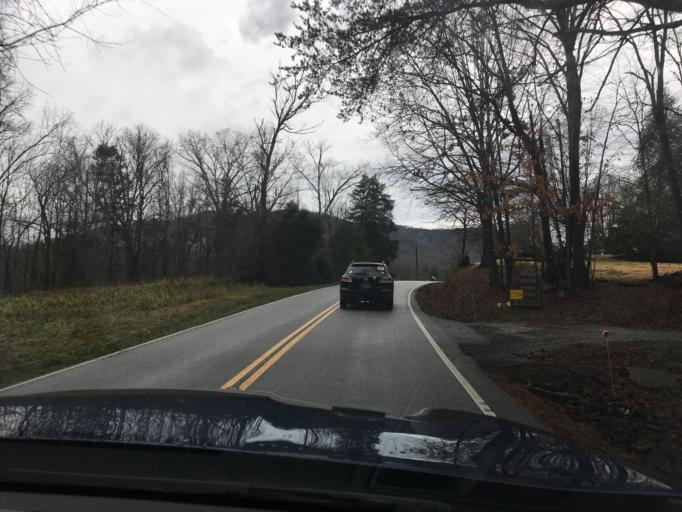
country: US
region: Tennessee
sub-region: McMinn County
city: Englewood
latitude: 35.3414
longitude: -84.3834
